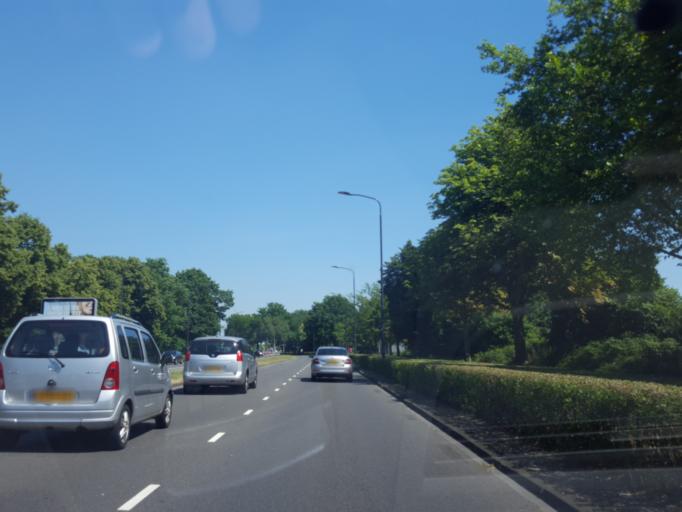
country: NL
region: North Brabant
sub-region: Gemeente Helmond
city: Helmond
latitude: 51.4769
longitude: 5.6638
